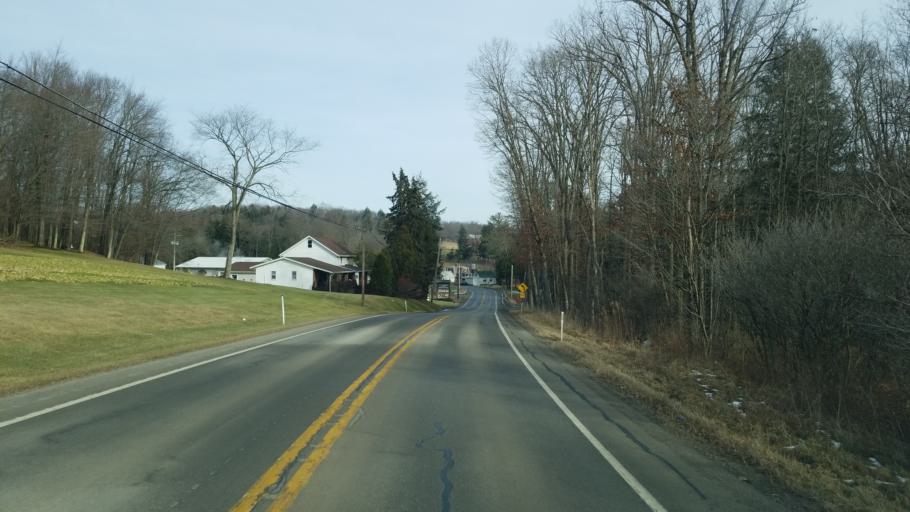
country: US
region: Pennsylvania
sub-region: Indiana County
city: Johnsonburg
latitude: 40.7573
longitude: -78.8692
